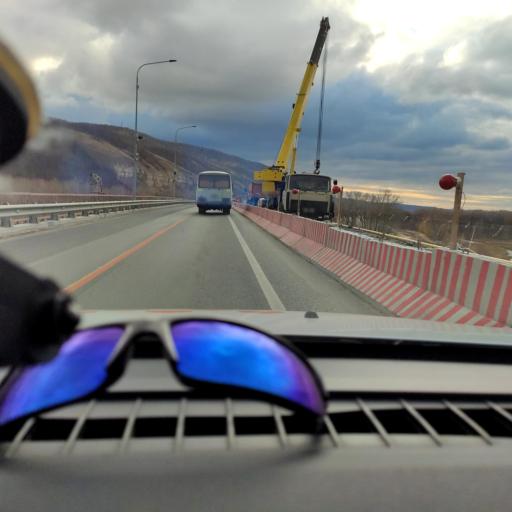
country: RU
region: Samara
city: Volzhskiy
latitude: 53.4125
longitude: 50.1362
